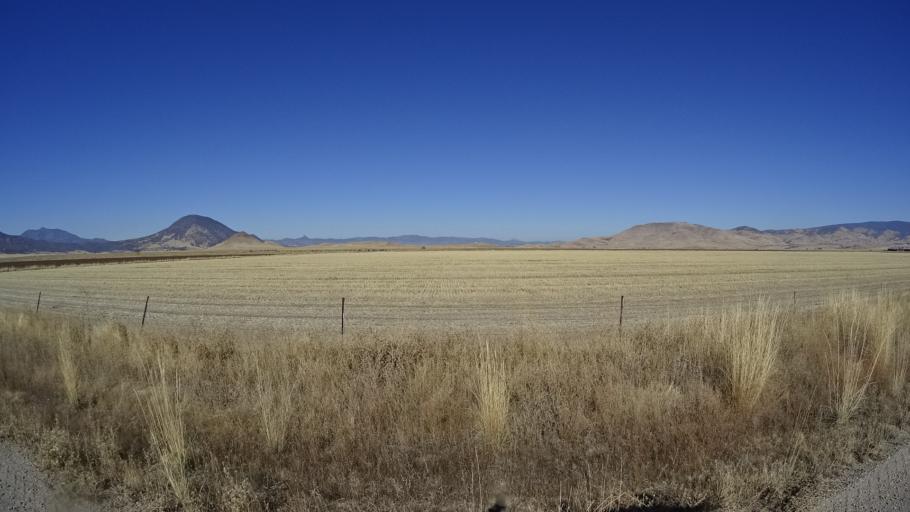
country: US
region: California
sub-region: Siskiyou County
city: Montague
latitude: 41.7865
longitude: -122.4499
